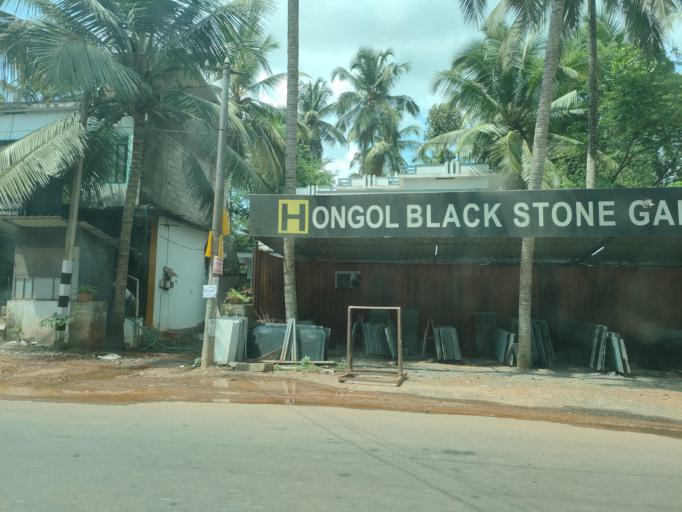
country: IN
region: Kerala
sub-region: Kozhikode
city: Mavoor
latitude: 11.2630
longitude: 75.9000
